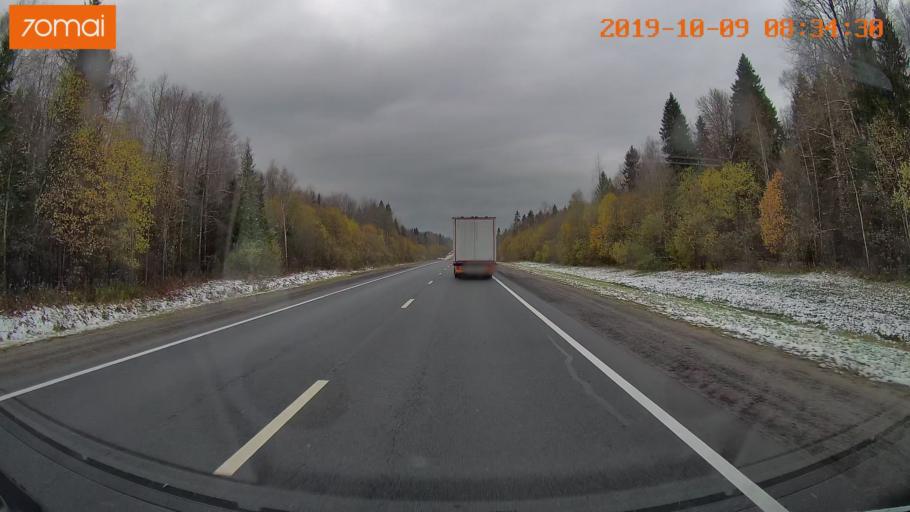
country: RU
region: Vologda
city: Gryazovets
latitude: 58.8973
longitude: 40.1853
